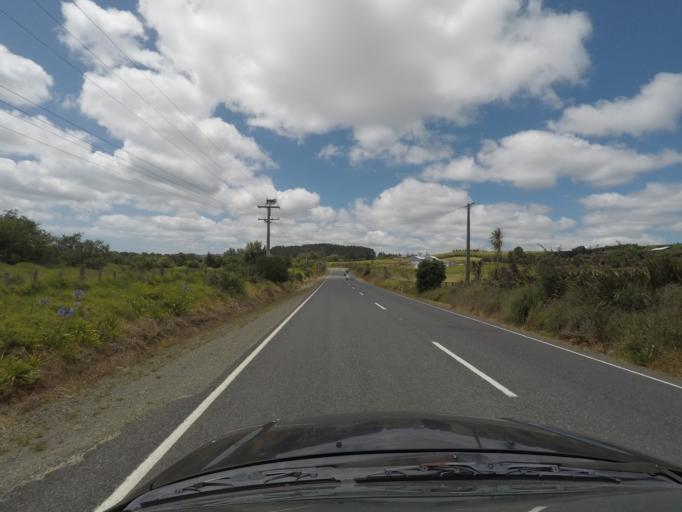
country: NZ
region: Northland
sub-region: Whangarei
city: Ruakaka
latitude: -36.0119
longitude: 174.4825
